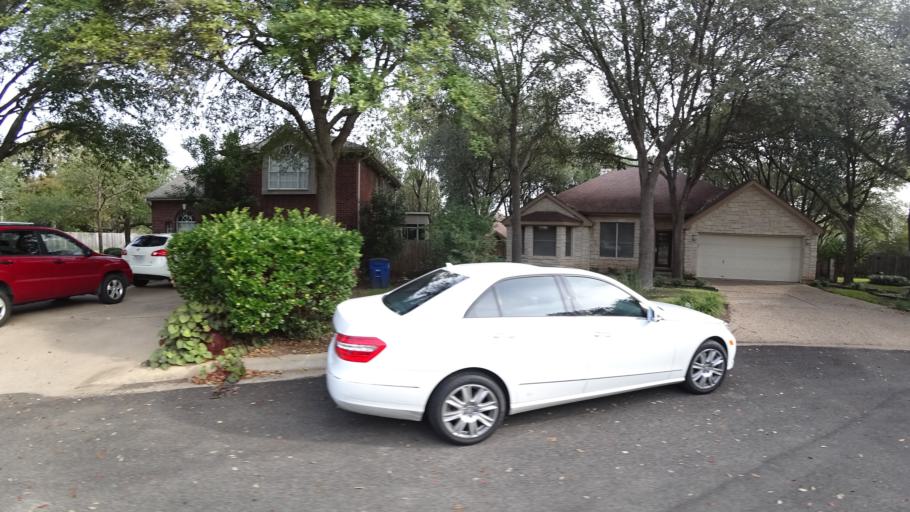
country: US
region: Texas
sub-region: Travis County
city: Shady Hollow
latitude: 30.1905
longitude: -97.8862
